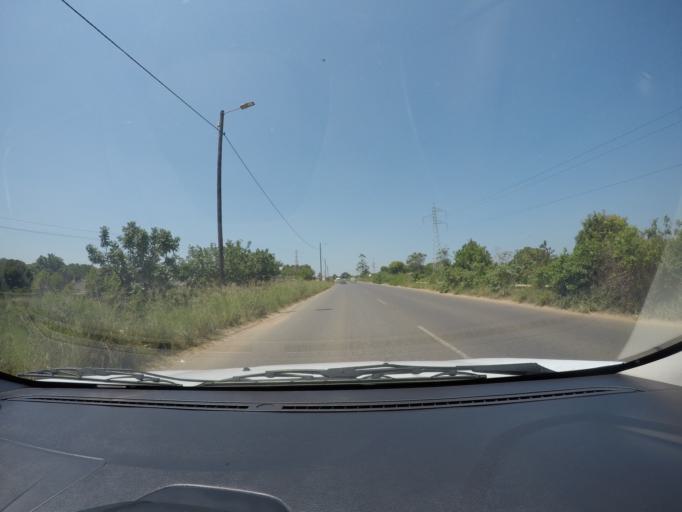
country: ZA
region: KwaZulu-Natal
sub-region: uThungulu District Municipality
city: eSikhawini
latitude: -28.8478
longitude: 31.9292
